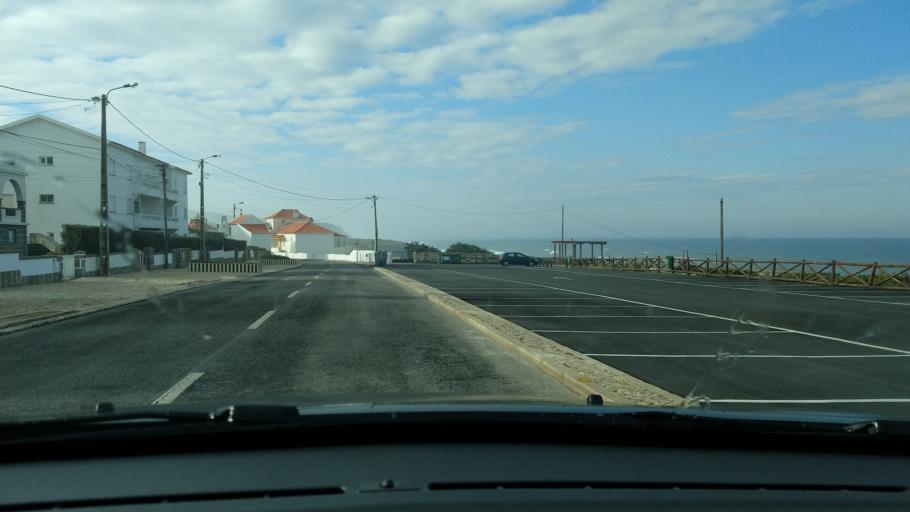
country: PT
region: Lisbon
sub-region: Sintra
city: Colares
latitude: 38.8290
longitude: -9.4689
